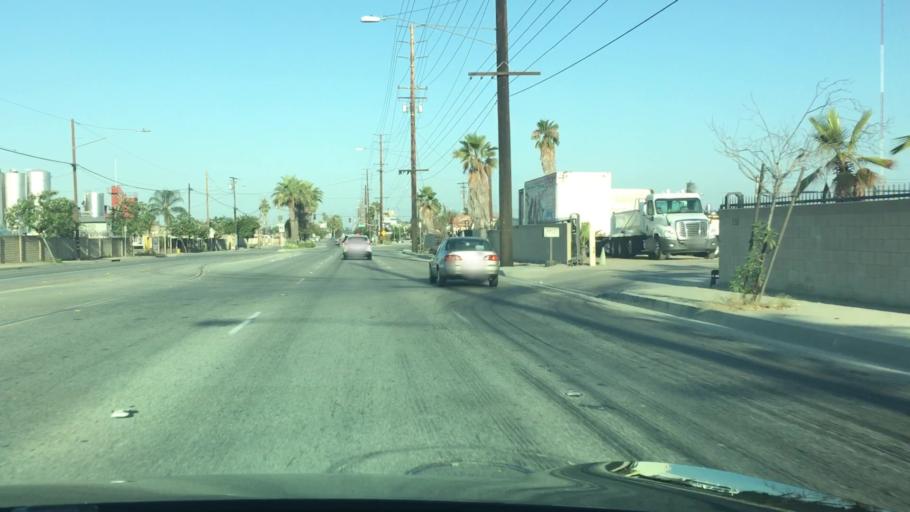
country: US
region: California
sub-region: Los Angeles County
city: Mayflower Village
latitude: 34.1124
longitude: -117.9965
